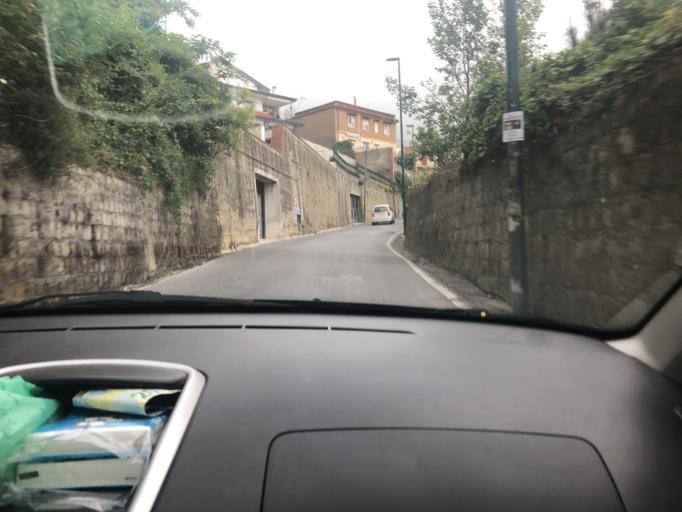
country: IT
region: Campania
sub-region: Provincia di Napoli
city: Torre Caracciolo
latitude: 40.8677
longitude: 14.1871
